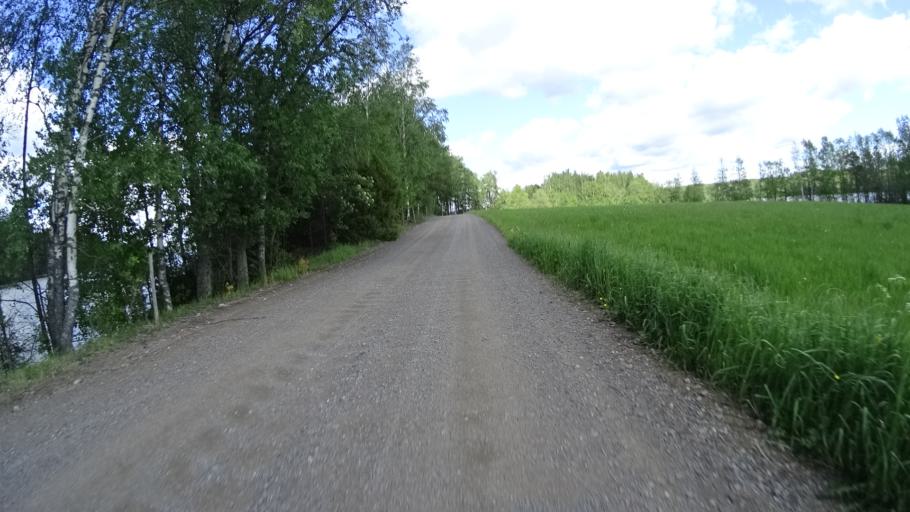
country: FI
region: Uusimaa
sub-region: Raaseporin
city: Pohja
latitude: 60.1238
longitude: 23.5993
